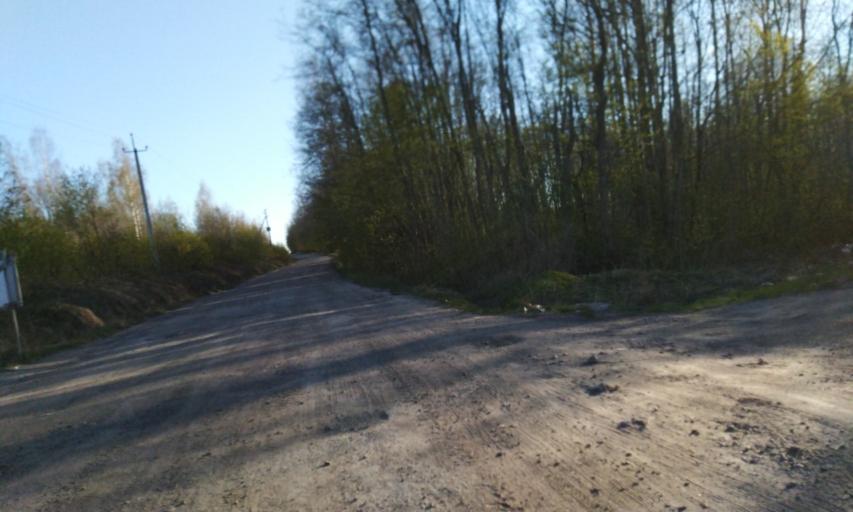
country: RU
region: Leningrad
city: Toksovo
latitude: 60.1482
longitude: 30.5803
